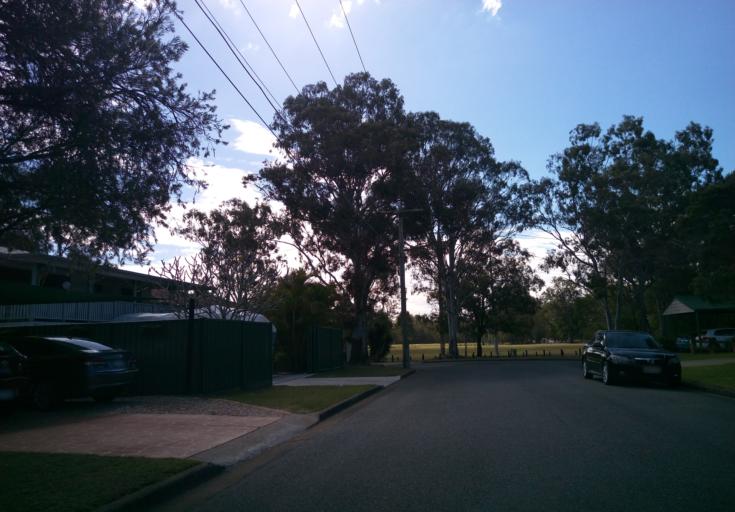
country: AU
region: Queensland
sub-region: Brisbane
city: Manly West
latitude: -27.4889
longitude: 153.2060
